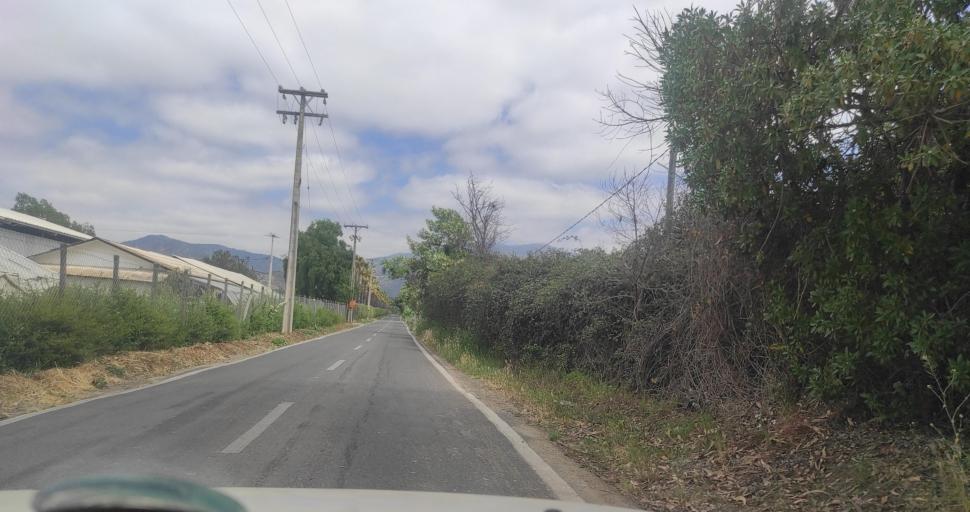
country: CL
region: Valparaiso
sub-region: Provincia de Marga Marga
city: Limache
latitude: -33.0272
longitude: -71.2291
